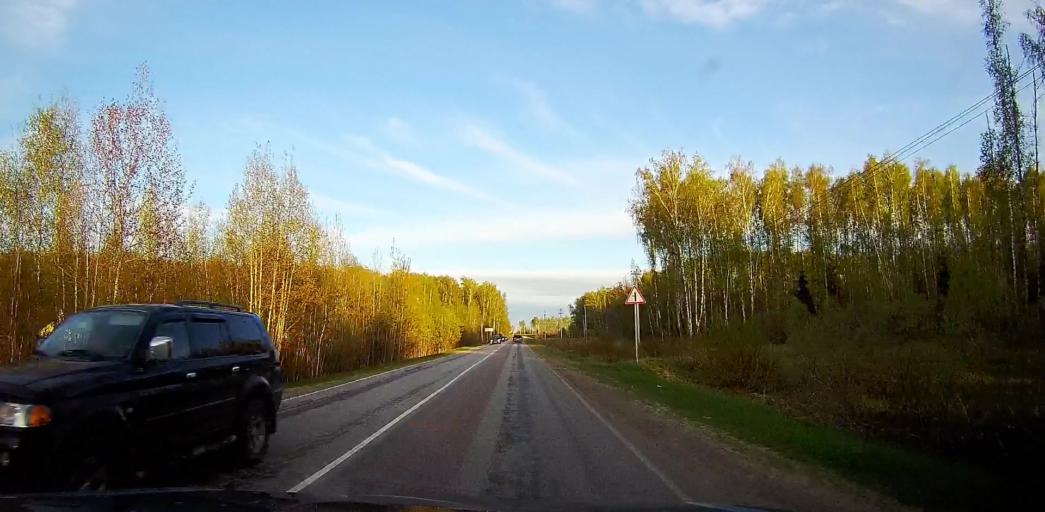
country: RU
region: Moskovskaya
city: Meshcherino
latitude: 55.2257
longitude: 38.3929
